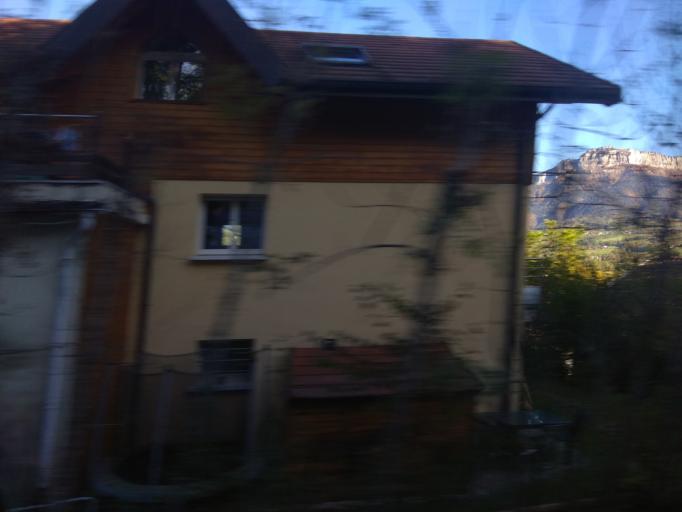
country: FR
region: Rhone-Alpes
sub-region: Departement de la Haute-Savoie
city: Saint-Martin-Bellevue
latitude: 45.9658
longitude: 6.1578
